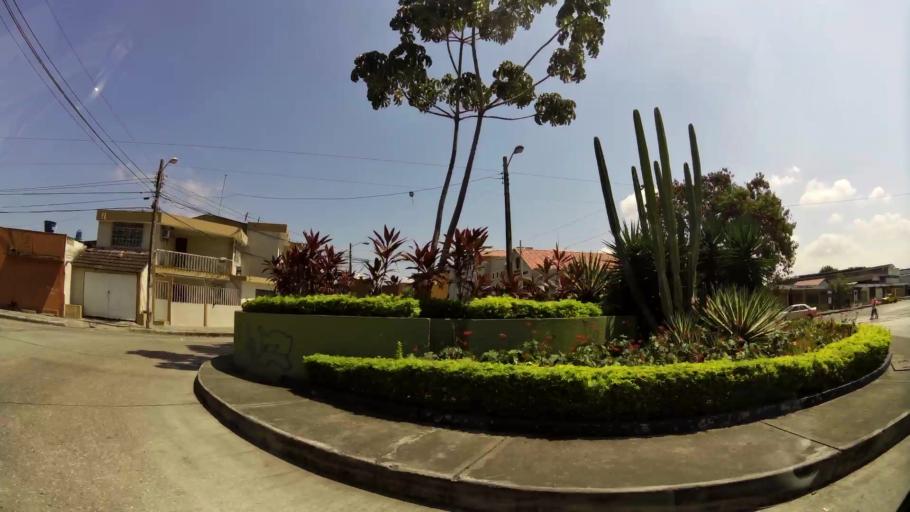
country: EC
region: Guayas
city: Guayaquil
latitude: -2.2340
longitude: -79.9012
